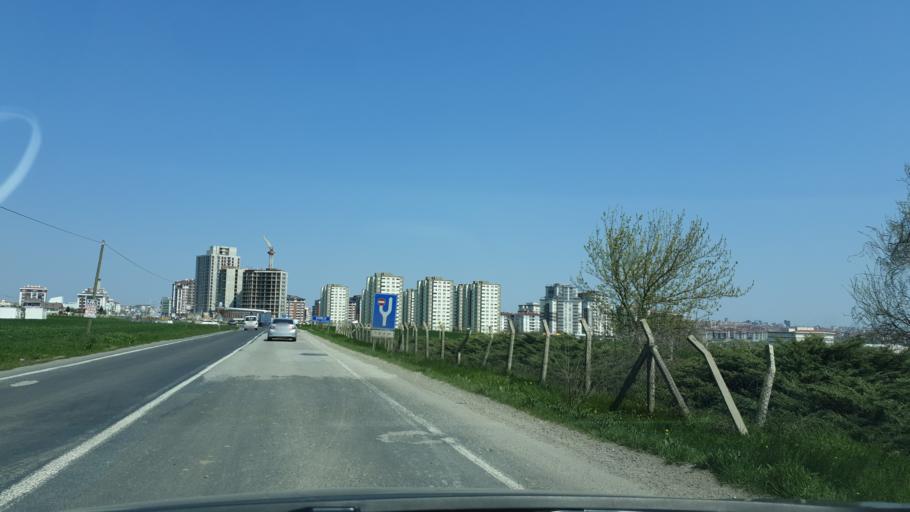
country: TR
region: Tekirdag
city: Corlu
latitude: 41.1464
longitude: 27.7732
